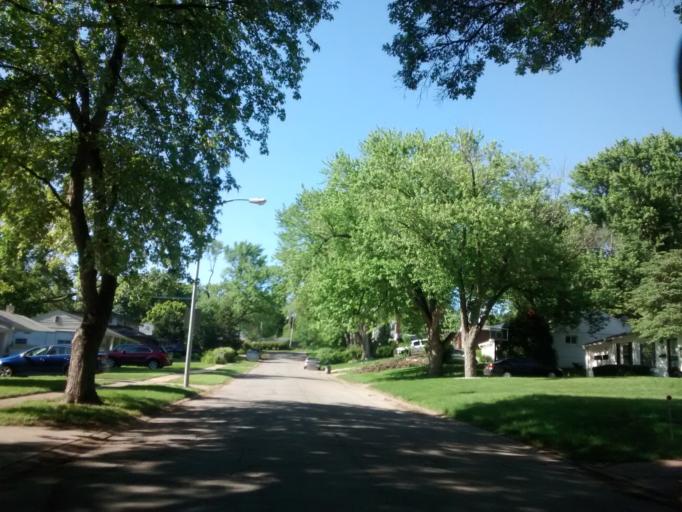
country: US
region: Nebraska
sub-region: Douglas County
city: Ralston
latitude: 41.2548
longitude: -96.0201
